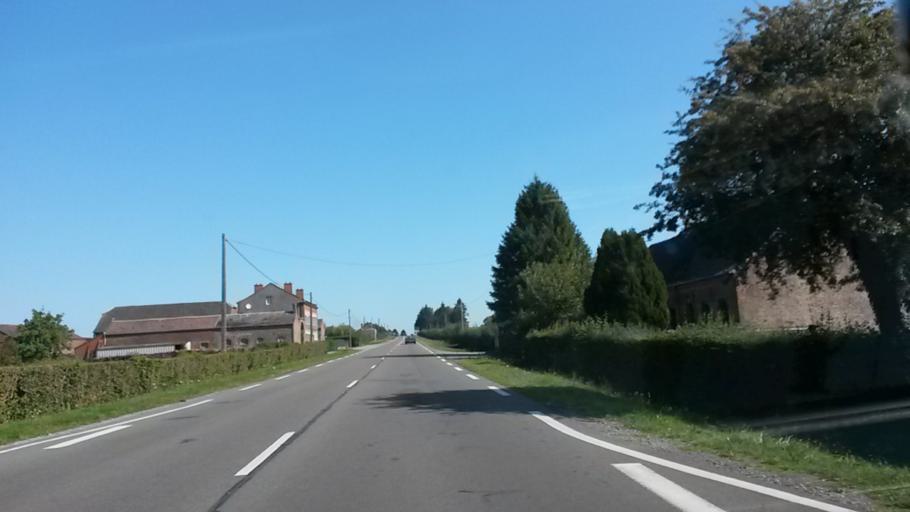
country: FR
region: Nord-Pas-de-Calais
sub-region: Departement du Nord
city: Avesnelles
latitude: 50.1487
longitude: 3.9508
